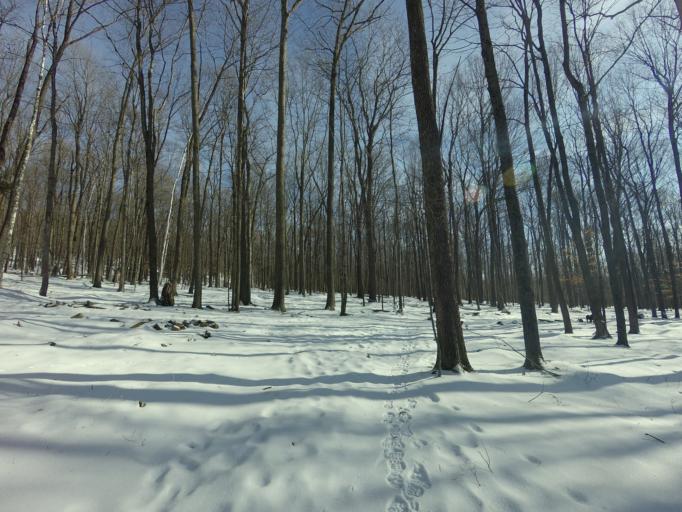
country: US
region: Wisconsin
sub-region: Marathon County
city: Rib Mountain
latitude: 44.9119
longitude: -89.6686
